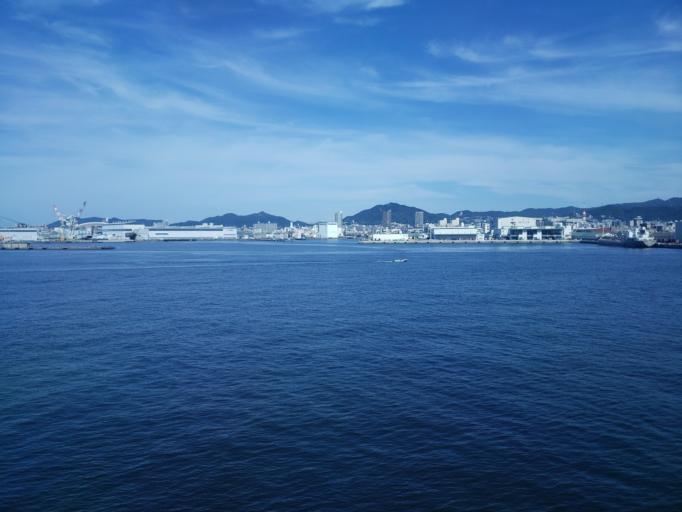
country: JP
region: Hyogo
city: Kobe
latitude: 34.6601
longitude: 135.1897
